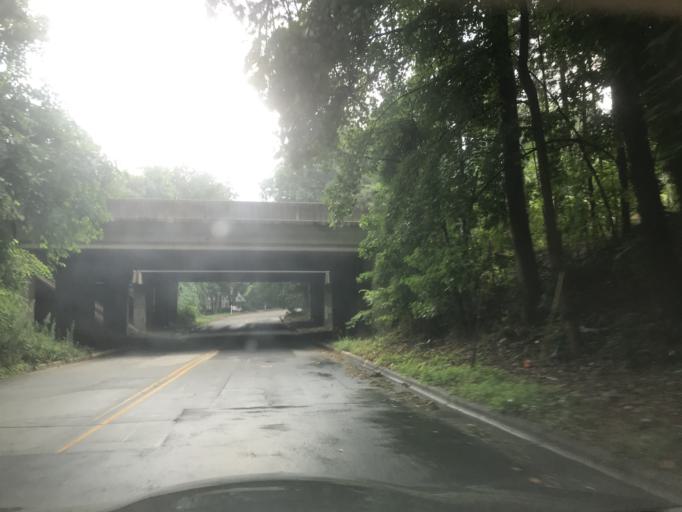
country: US
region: North Carolina
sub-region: Wake County
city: West Raleigh
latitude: 35.8371
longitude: -78.6562
